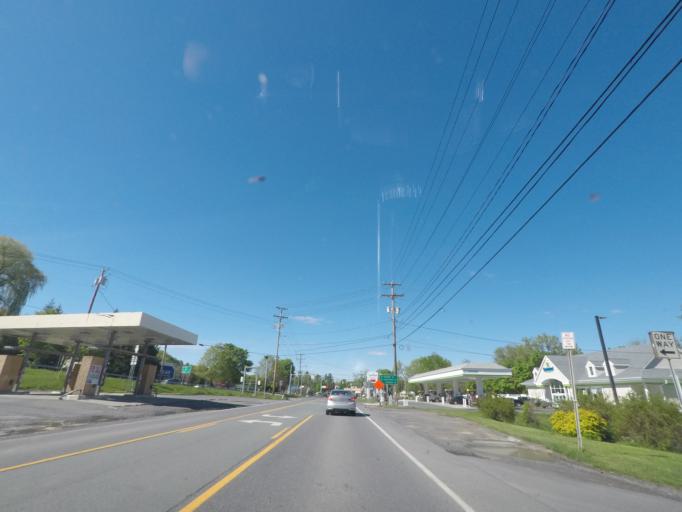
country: US
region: New York
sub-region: Albany County
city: Ravena
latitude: 42.4673
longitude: -73.8163
